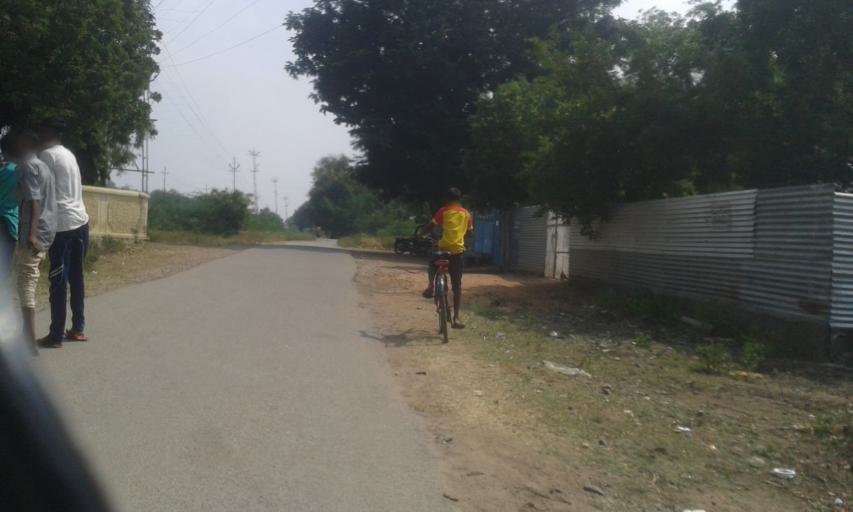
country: IN
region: Karnataka
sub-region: Raichur
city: Lingsugur
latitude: 16.1956
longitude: 76.6593
